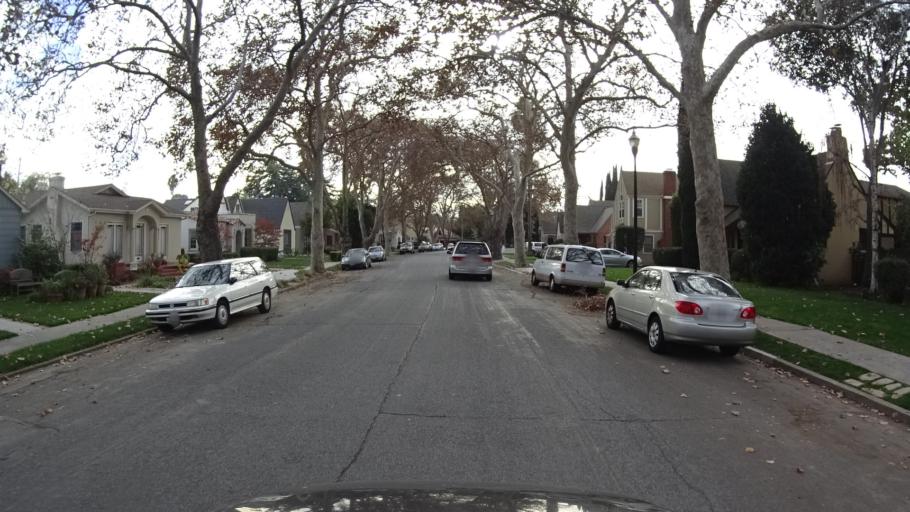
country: US
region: California
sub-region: Santa Clara County
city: Buena Vista
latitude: 37.3305
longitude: -121.9176
